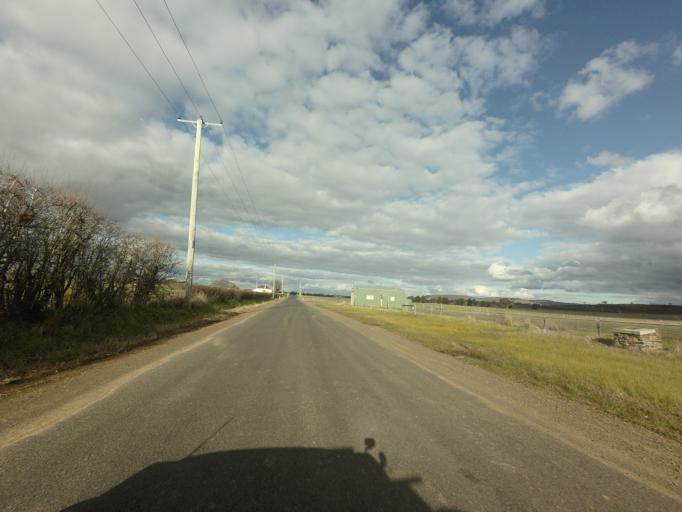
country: AU
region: Tasmania
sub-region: Northern Midlands
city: Longford
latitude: -41.8598
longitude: 147.2448
